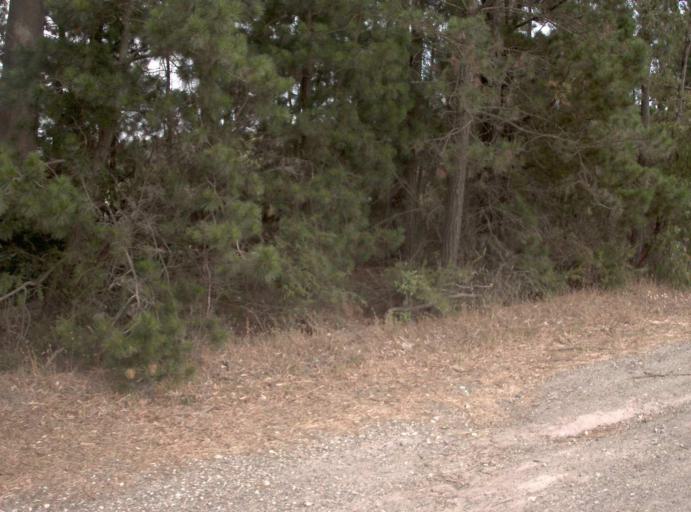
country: AU
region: Victoria
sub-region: Latrobe
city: Traralgon
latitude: -38.1312
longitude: 146.4719
